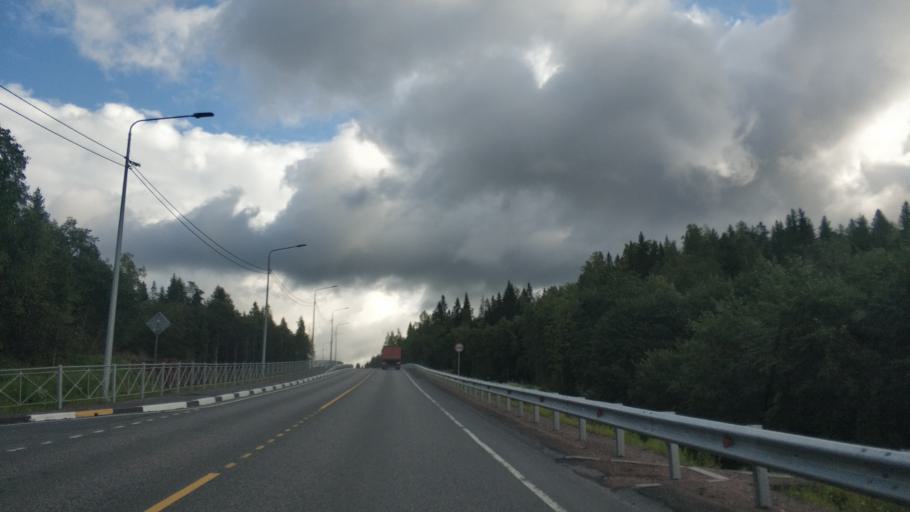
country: RU
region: Republic of Karelia
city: Ruskeala
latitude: 61.9421
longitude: 30.5918
